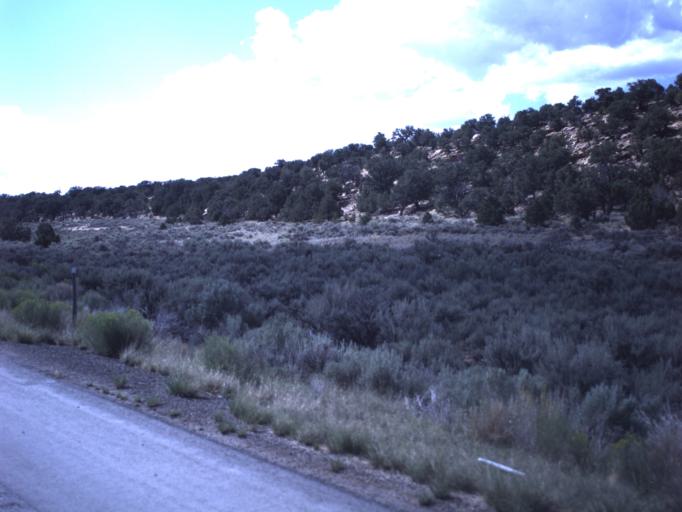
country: US
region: Utah
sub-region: Duchesne County
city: Duchesne
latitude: 40.1804
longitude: -110.6191
